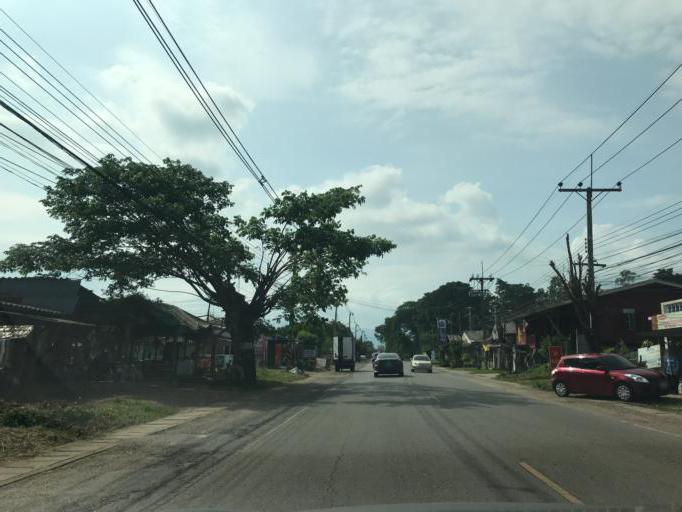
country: TH
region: Phayao
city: Chiang Kham
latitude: 19.5173
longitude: 100.3123
